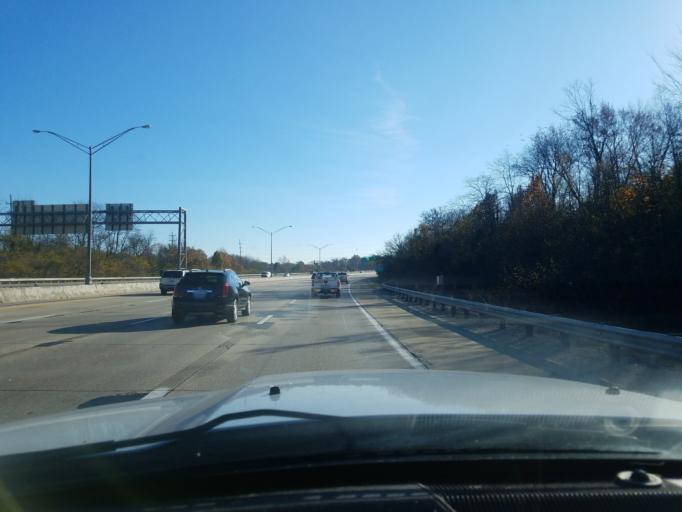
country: US
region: Kentucky
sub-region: Kenton County
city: Crestview Hills
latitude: 39.0315
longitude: -84.5854
